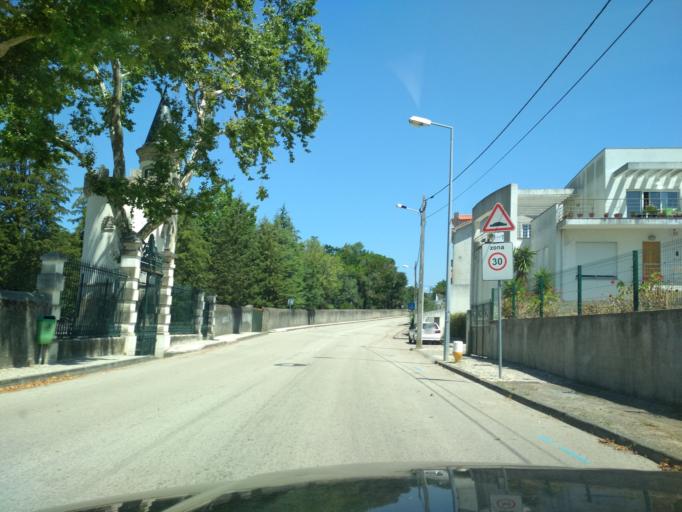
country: PT
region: Coimbra
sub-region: Condeixa-A-Nova
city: Condeixa-a-Nova
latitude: 40.1407
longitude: -8.4682
